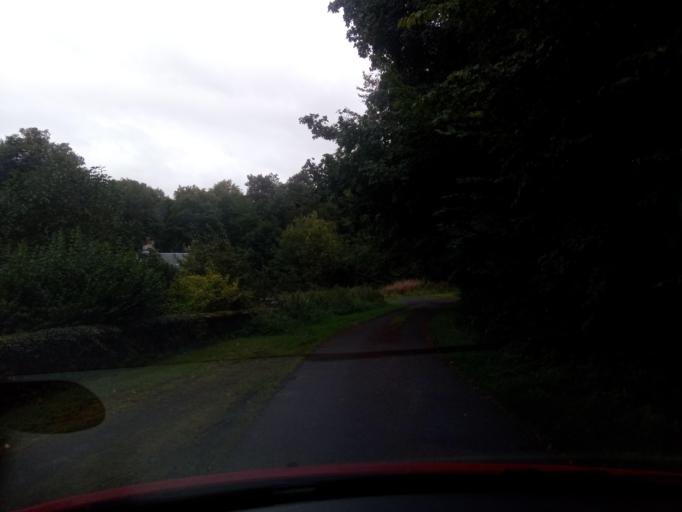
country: GB
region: Scotland
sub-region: The Scottish Borders
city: Jedburgh
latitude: 55.5092
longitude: -2.5398
